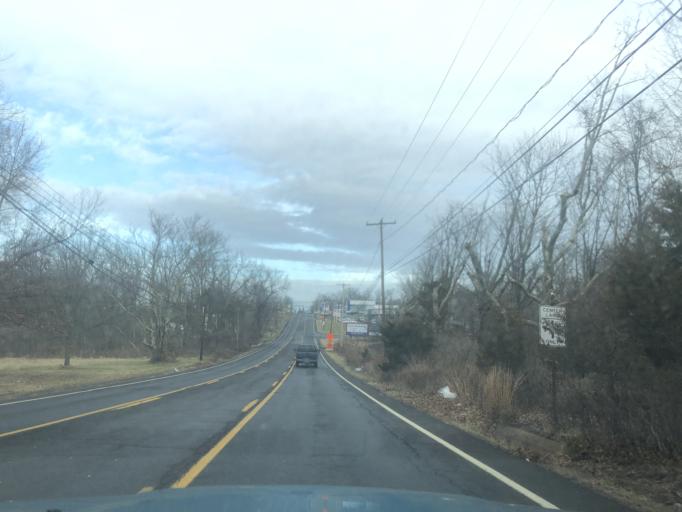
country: US
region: Pennsylvania
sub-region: Bucks County
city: Sellersville
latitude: 40.3413
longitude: -75.3035
